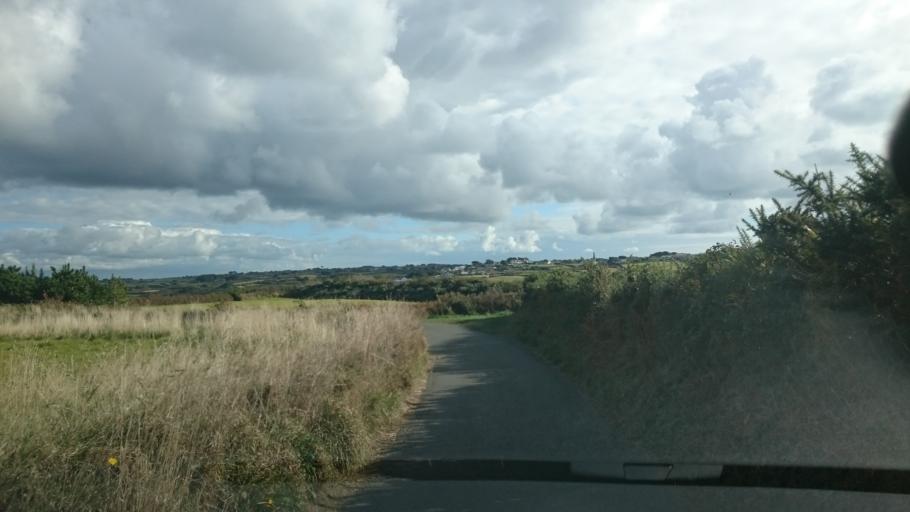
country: GG
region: St Peter Port
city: Saint Peter Port
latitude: 49.4310
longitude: -2.6665
